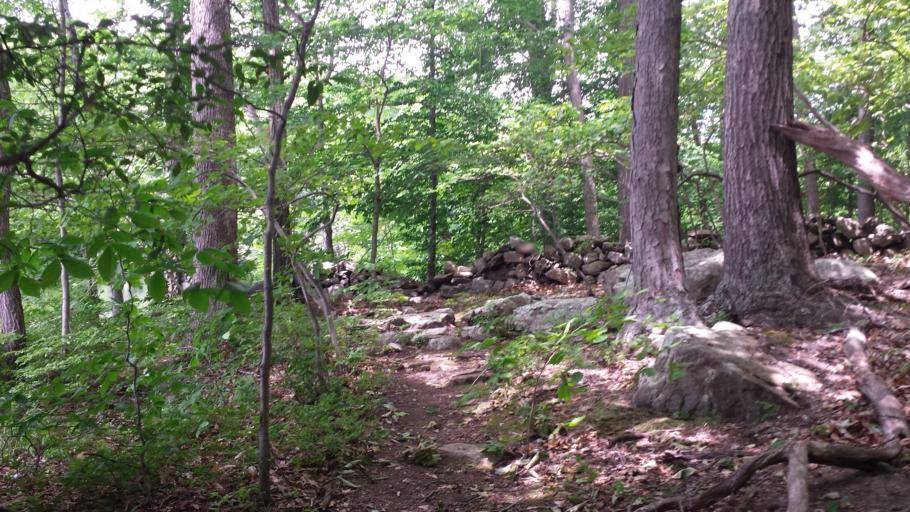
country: US
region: New York
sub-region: Putnam County
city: Peach Lake
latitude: 41.3106
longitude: -73.5677
